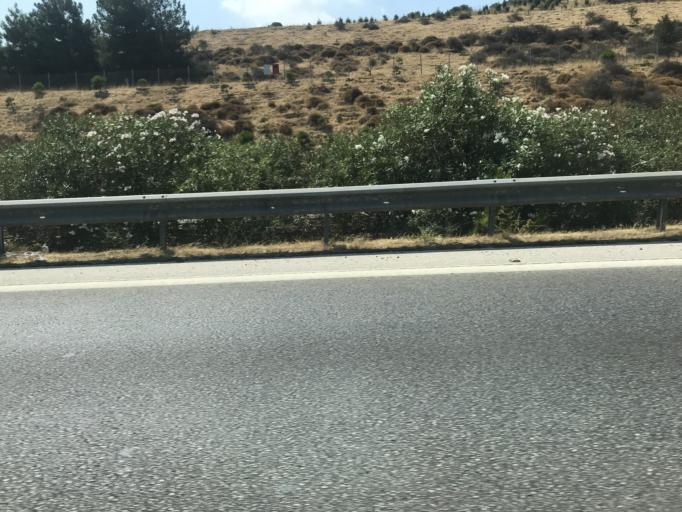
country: TR
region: Izmir
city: Urla
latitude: 38.3708
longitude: 26.9223
